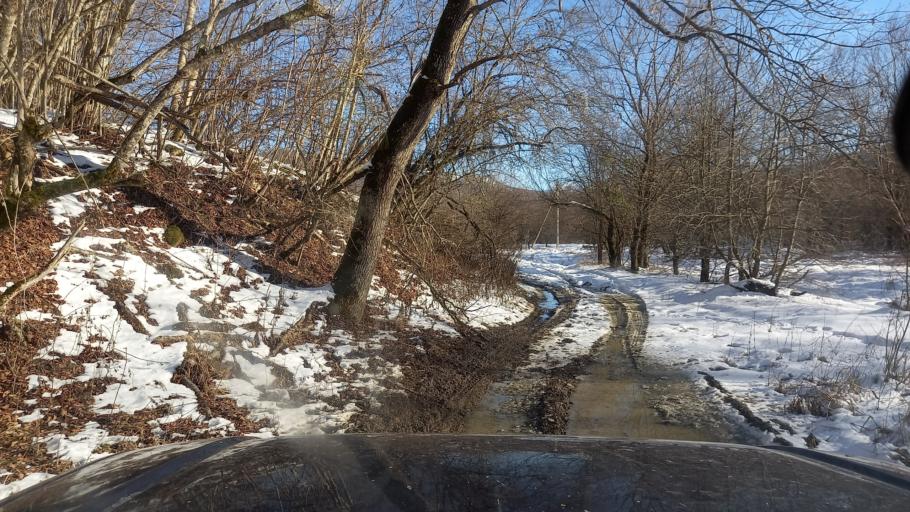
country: RU
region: Adygeya
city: Kamennomostskiy
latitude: 44.2048
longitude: 40.1511
